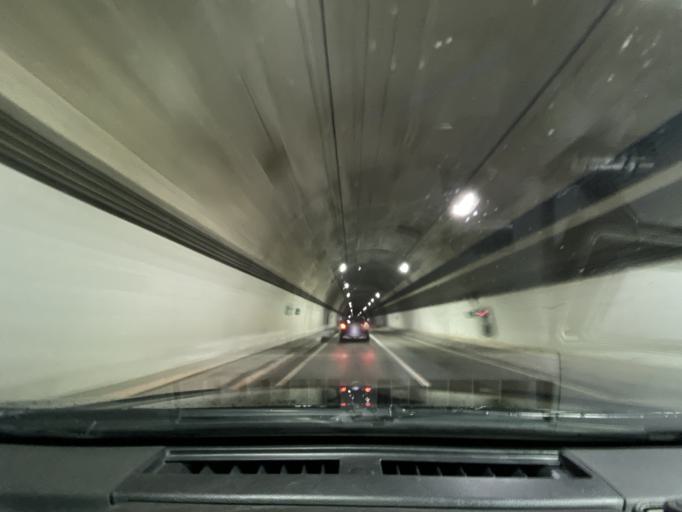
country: JP
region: Hokkaido
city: Ishikari
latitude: 43.4478
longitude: 141.4108
